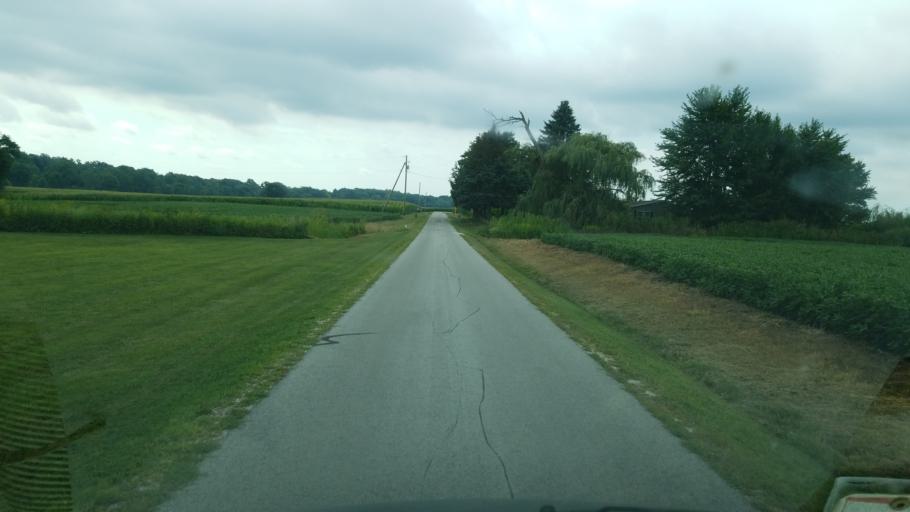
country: US
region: Ohio
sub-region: Sandusky County
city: Green Springs
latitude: 41.2190
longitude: -83.1357
